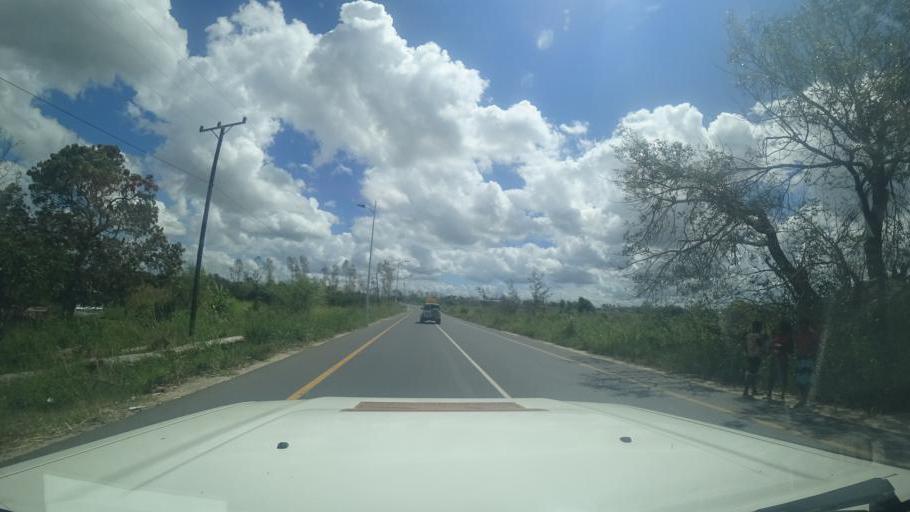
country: MZ
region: Sofala
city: Dondo
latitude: -19.5738
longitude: 34.7180
